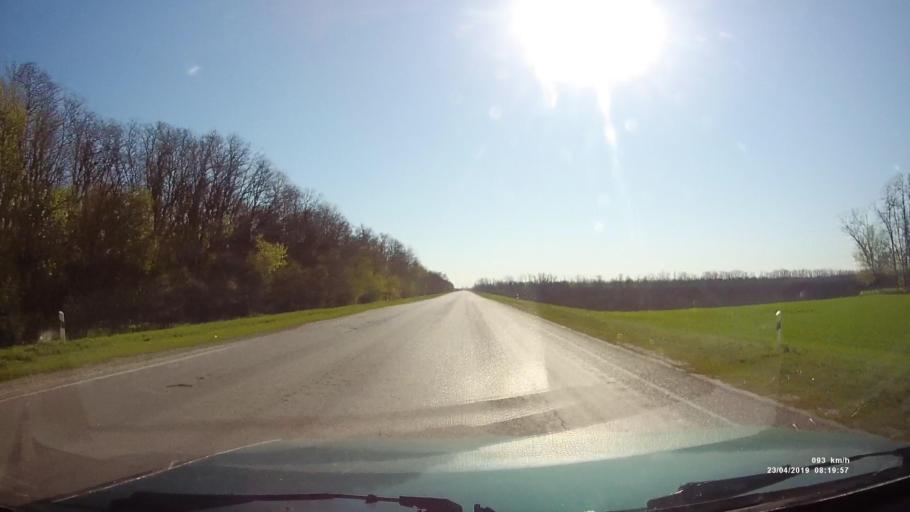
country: RU
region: Rostov
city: Tselina
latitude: 46.5375
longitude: 40.8601
